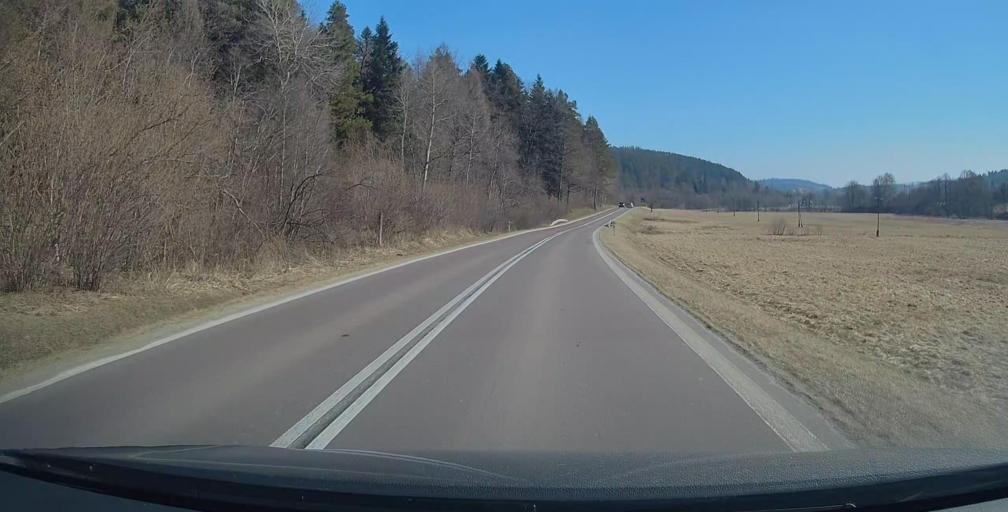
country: PL
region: Subcarpathian Voivodeship
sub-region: Powiat przemyski
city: Bircza
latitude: 49.5899
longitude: 22.5273
